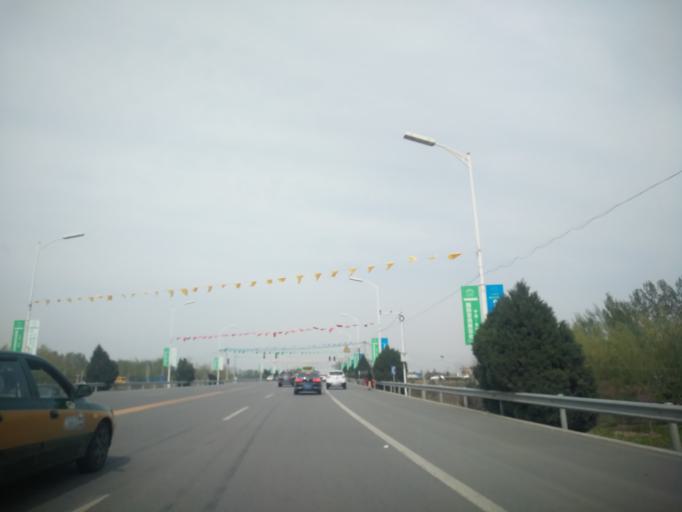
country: CN
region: Beijing
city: Xiji
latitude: 39.7767
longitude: 116.9800
